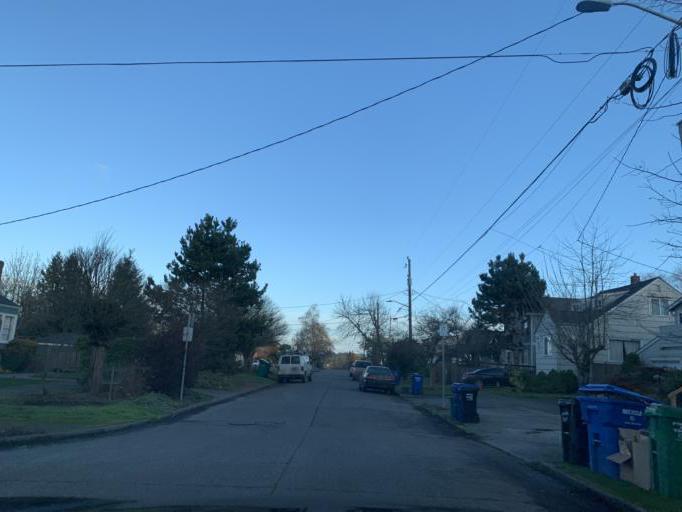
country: US
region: Washington
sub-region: King County
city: Seattle
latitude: 47.5810
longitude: -122.3083
